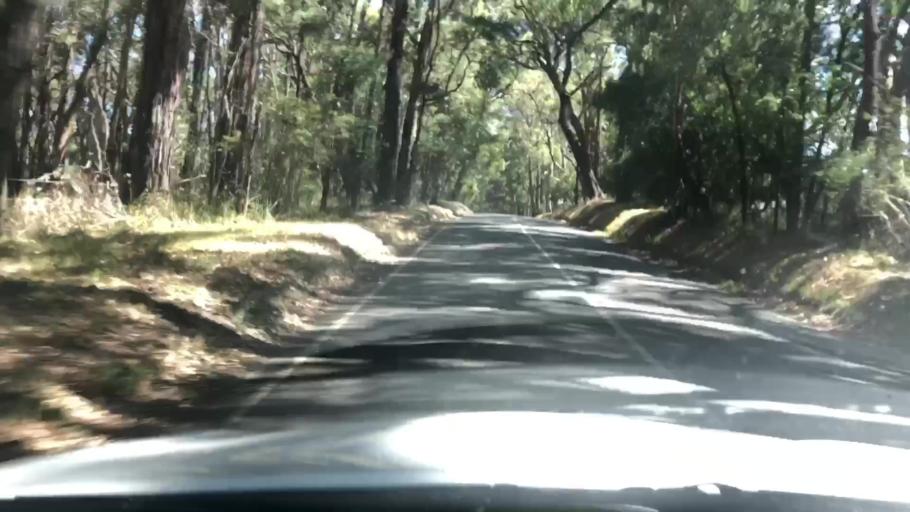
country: AU
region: Victoria
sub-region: Yarra Ranges
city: Macclesfield
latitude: -37.8579
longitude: 145.4807
